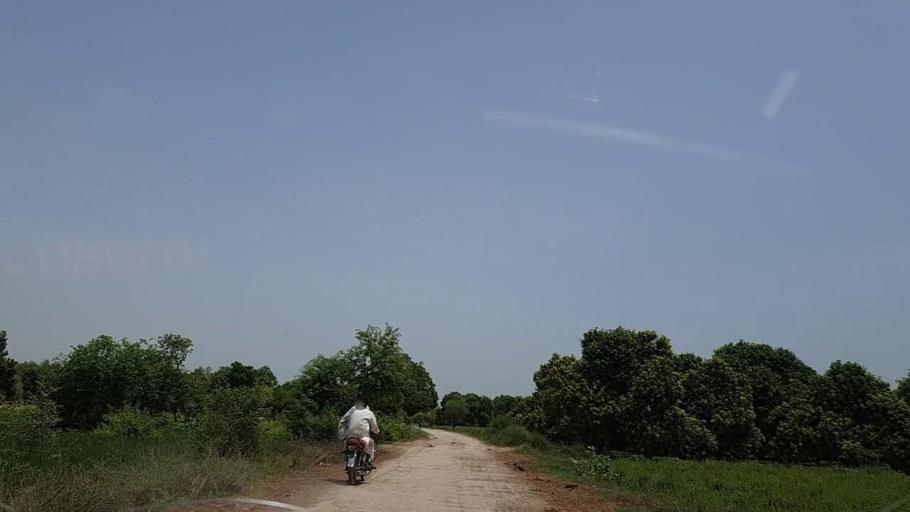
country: PK
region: Sindh
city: Tharu Shah
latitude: 26.9614
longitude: 68.0319
